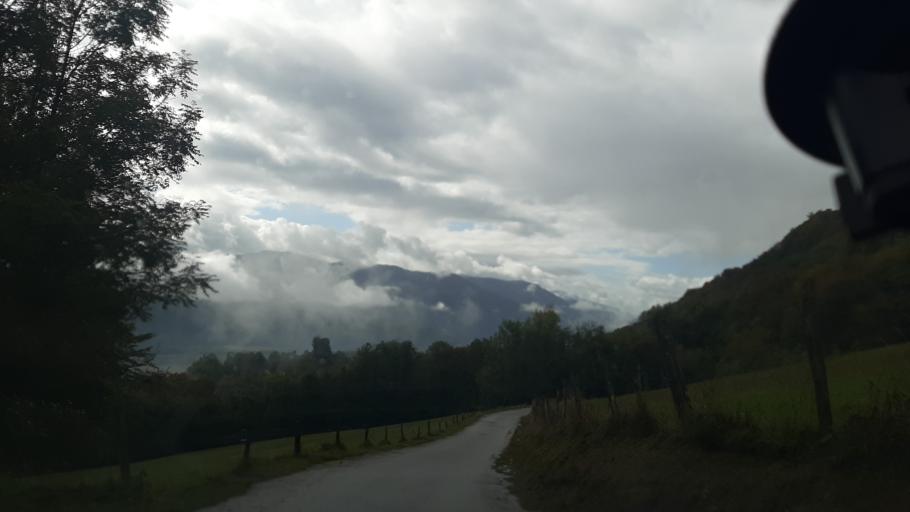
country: FR
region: Rhone-Alpes
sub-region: Departement de la Savoie
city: Gresy-sur-Isere
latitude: 45.6262
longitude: 6.2773
